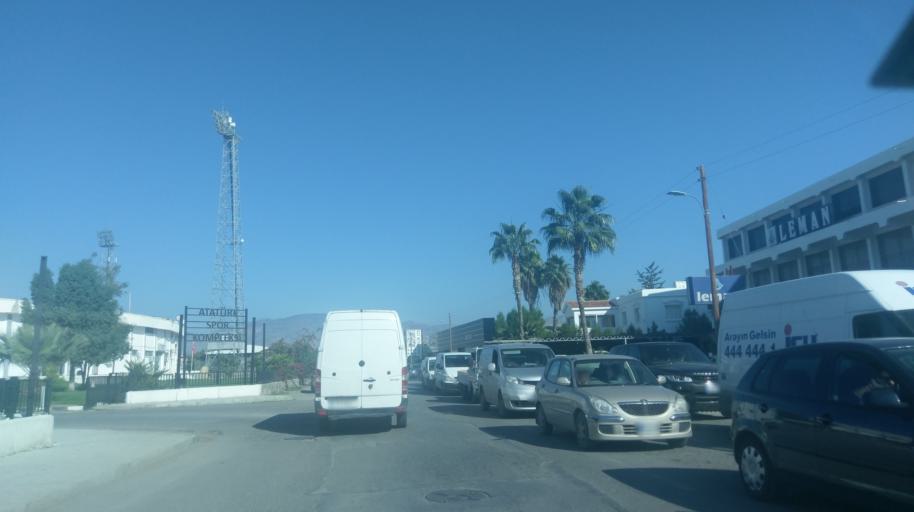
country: CY
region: Lefkosia
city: Nicosia
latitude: 35.2125
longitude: 33.3391
